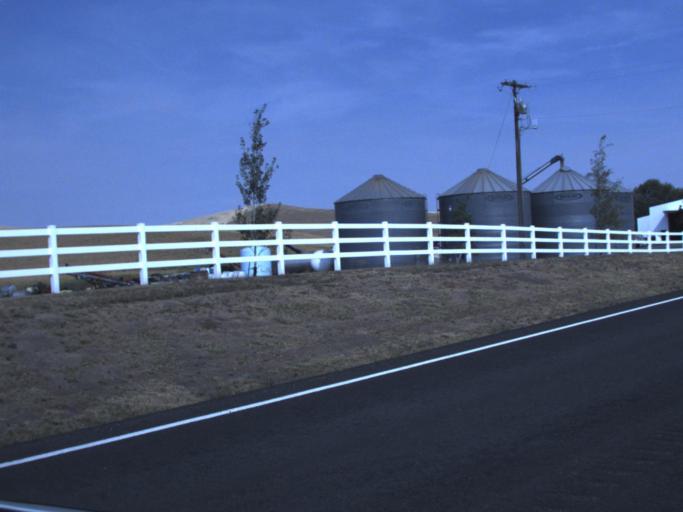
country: US
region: Washington
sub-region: Whitman County
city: Pullman
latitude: 46.7678
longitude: -117.1659
